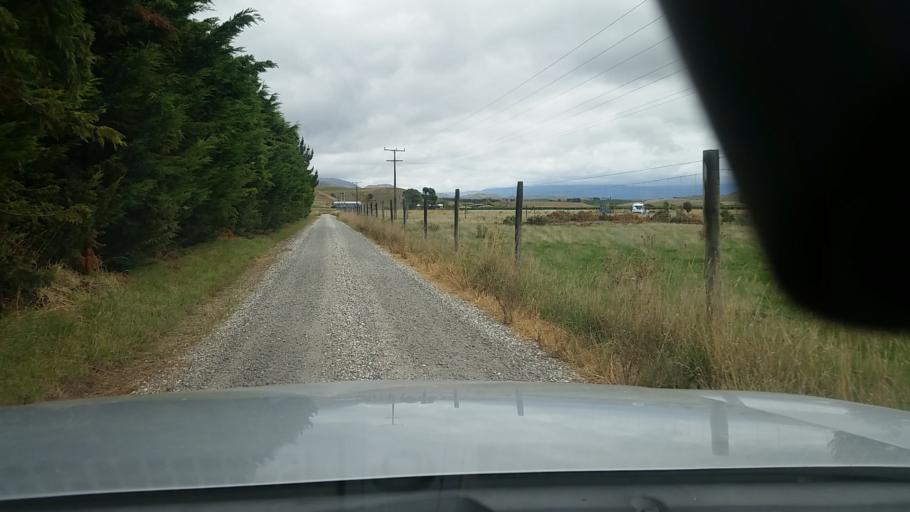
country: NZ
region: Marlborough
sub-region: Marlborough District
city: Blenheim
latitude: -41.6996
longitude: 174.1183
